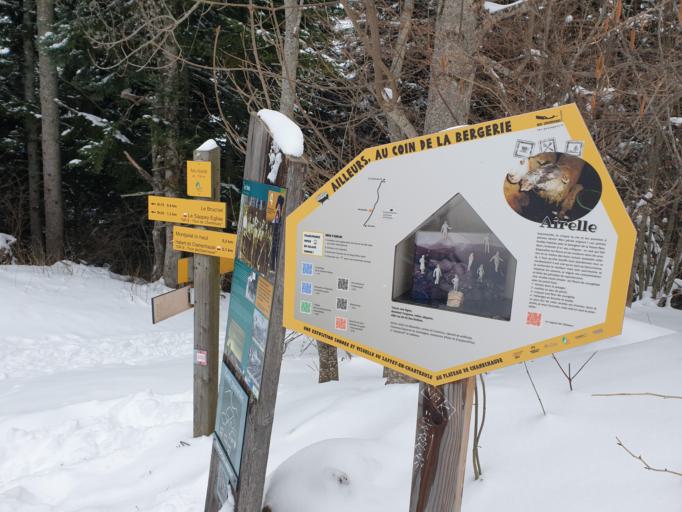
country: FR
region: Rhone-Alpes
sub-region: Departement de l'Isere
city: Le Sappey-en-Chartreuse
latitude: 45.2681
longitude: 5.7870
